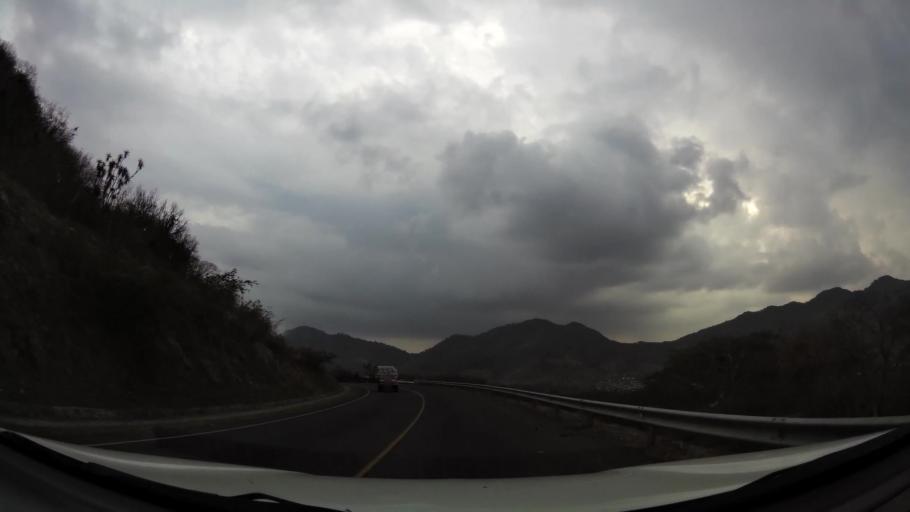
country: NI
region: Jinotega
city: Jinotega
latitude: 13.0638
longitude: -85.9920
